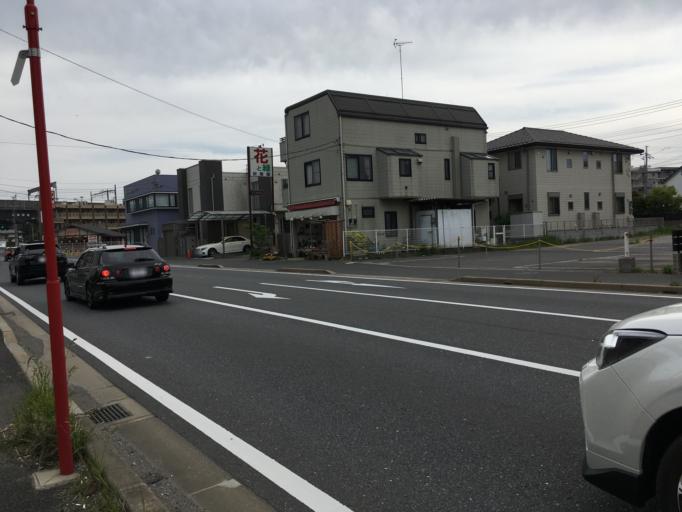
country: JP
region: Chiba
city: Matsudo
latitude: 35.7717
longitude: 139.9420
